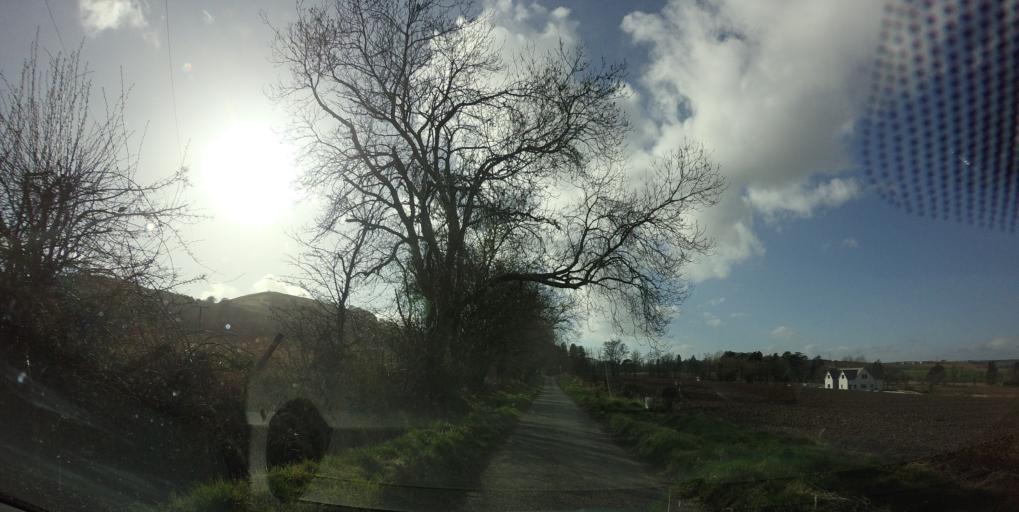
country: GB
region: Scotland
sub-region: Perth and Kinross
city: Bridge of Earn
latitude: 56.3306
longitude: -3.4273
